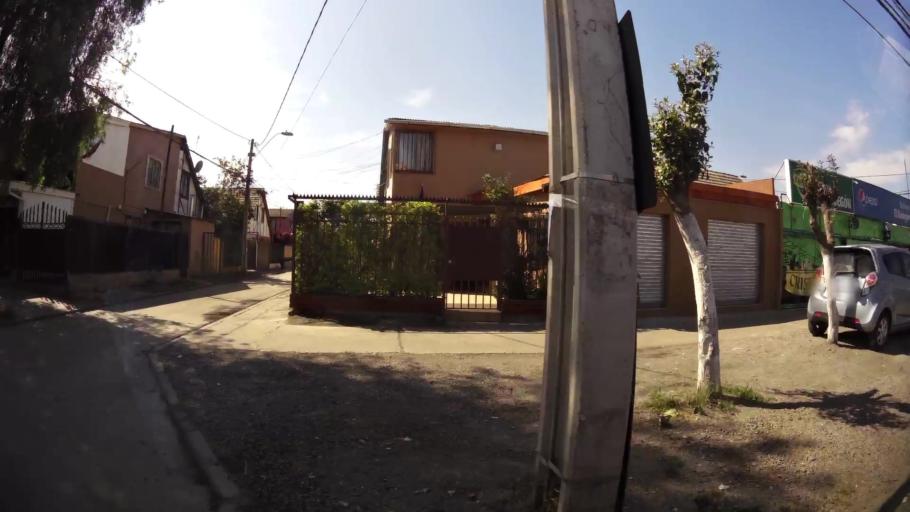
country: CL
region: Santiago Metropolitan
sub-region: Provincia de Santiago
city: Lo Prado
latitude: -33.4713
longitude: -70.7482
